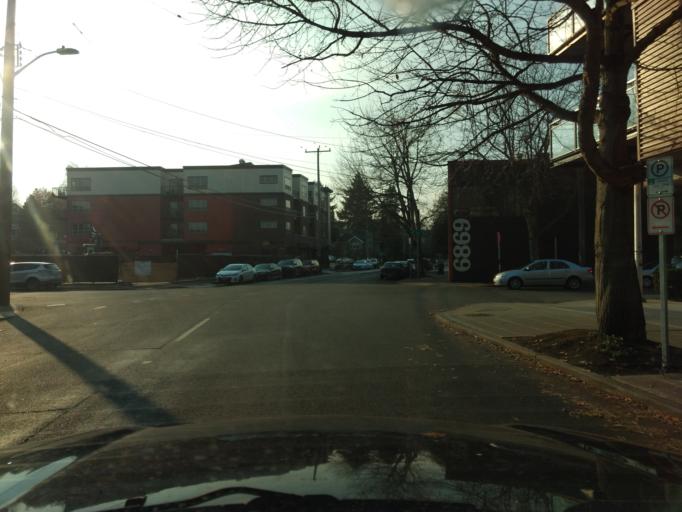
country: US
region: Washington
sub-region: King County
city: Seattle
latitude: 47.6780
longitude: -122.3260
